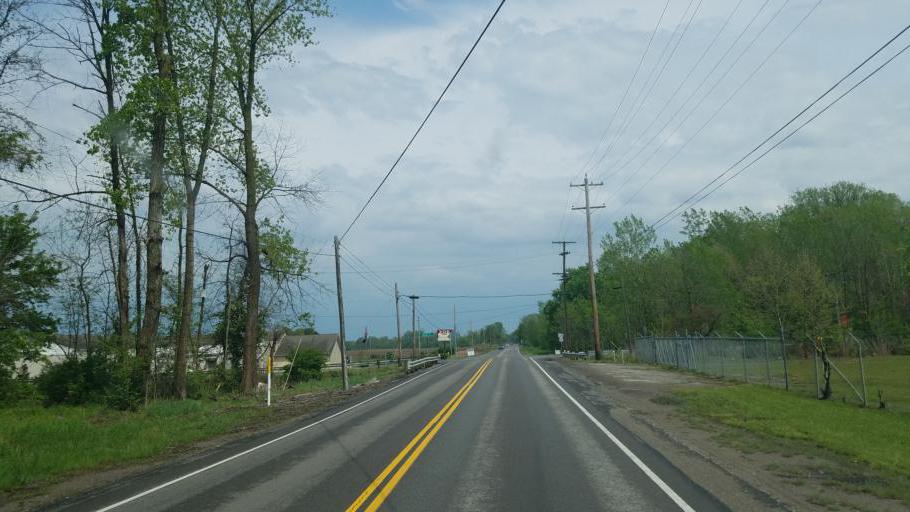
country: US
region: Ohio
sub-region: Fairfield County
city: Millersport
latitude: 39.9273
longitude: -82.5195
